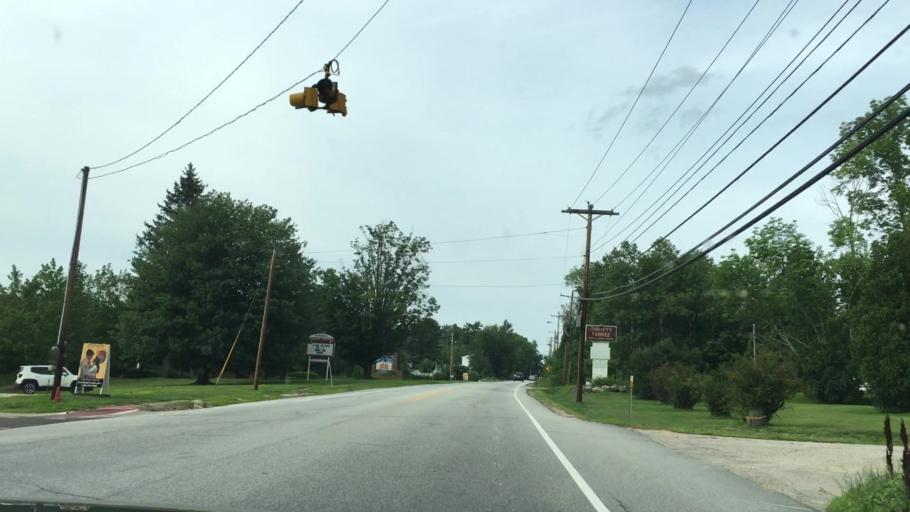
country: US
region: New Hampshire
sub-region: Belknap County
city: Meredith
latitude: 43.6656
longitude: -71.4902
